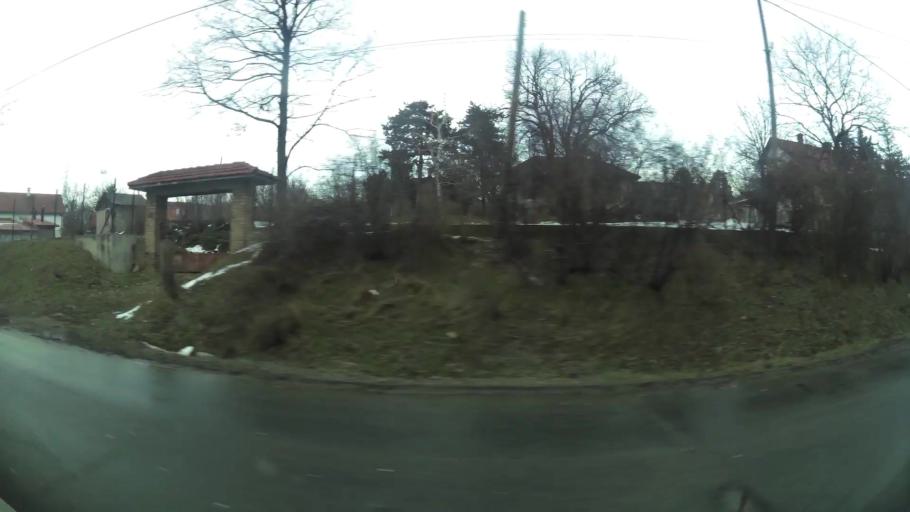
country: RS
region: Central Serbia
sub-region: Belgrade
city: Vozdovac
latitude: 44.7441
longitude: 20.4803
